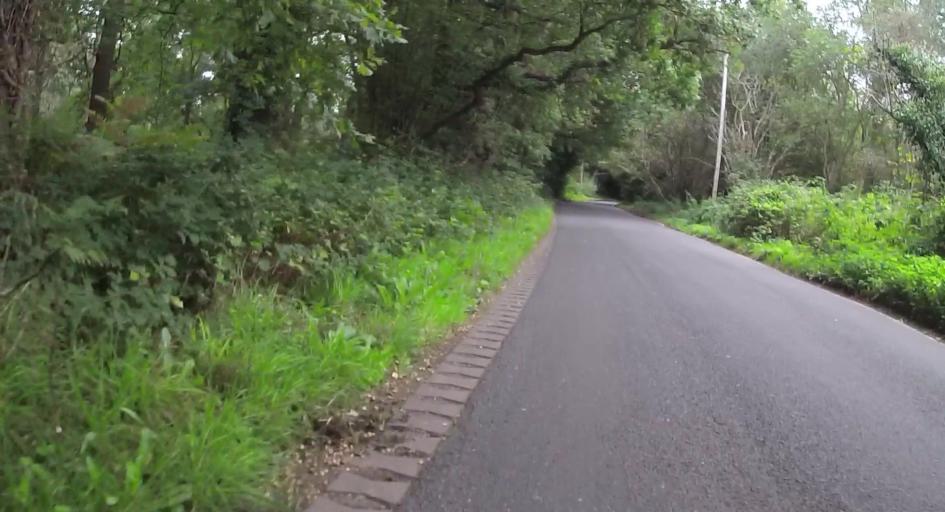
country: GB
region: England
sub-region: Surrey
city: West Byfleet
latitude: 51.3220
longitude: -0.4947
